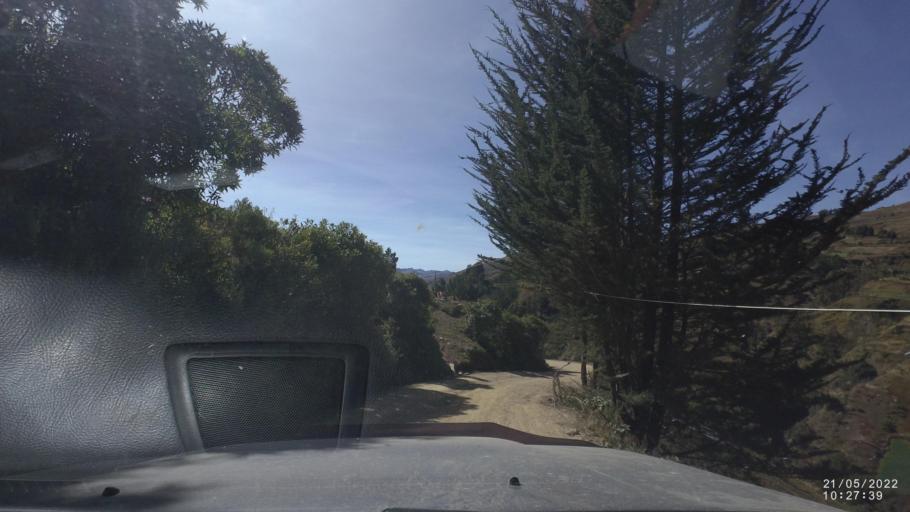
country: BO
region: Cochabamba
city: Colomi
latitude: -17.3231
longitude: -65.9436
